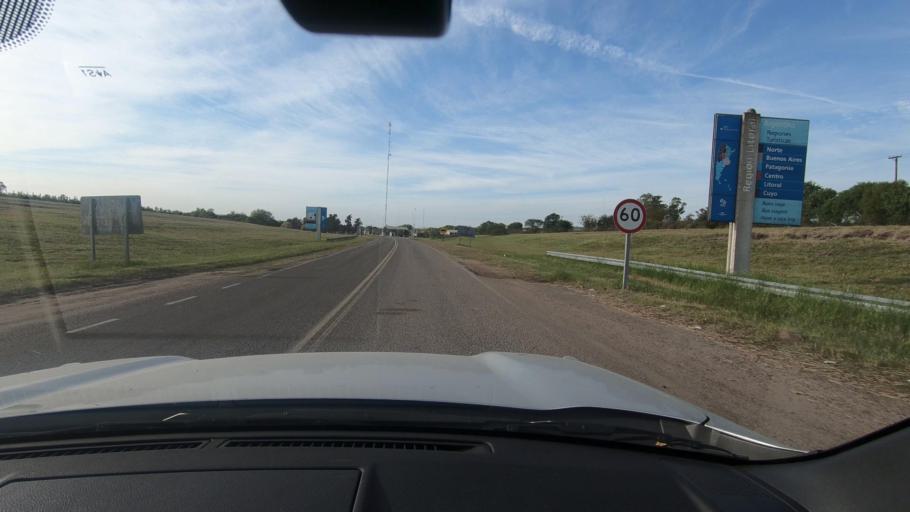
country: AR
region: Entre Rios
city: Colon
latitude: -32.2479
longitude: -58.1986
